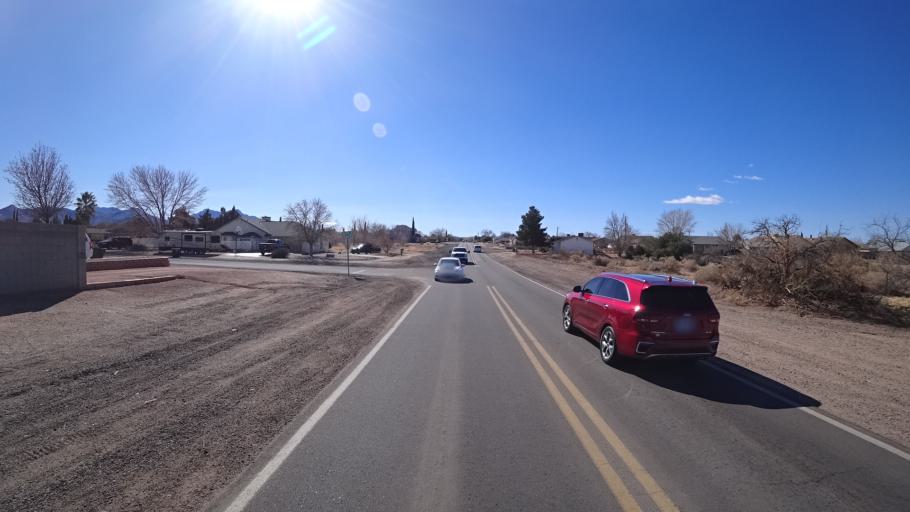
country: US
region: Arizona
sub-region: Mohave County
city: Kingman
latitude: 35.2078
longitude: -114.0114
